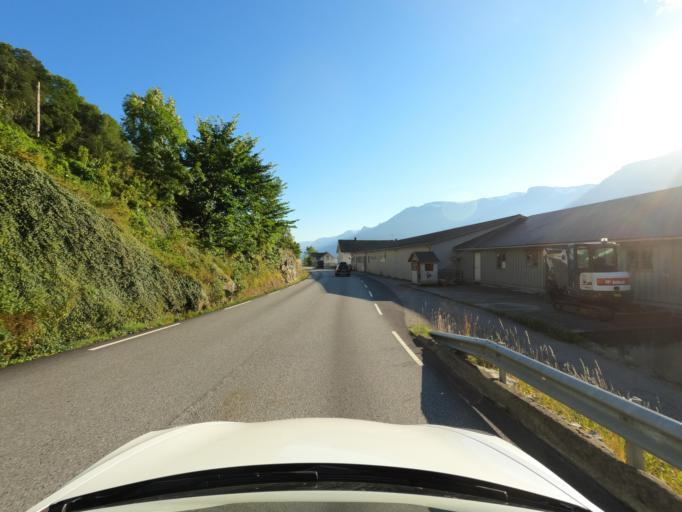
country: NO
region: Hordaland
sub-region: Ullensvang
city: Kinsarvik
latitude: 60.2780
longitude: 6.6196
